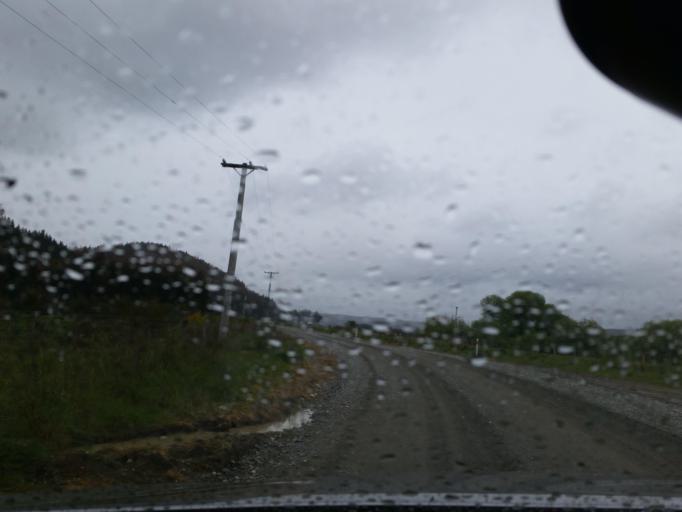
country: NZ
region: Southland
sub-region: Southland District
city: Riverton
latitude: -45.9812
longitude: 167.5991
